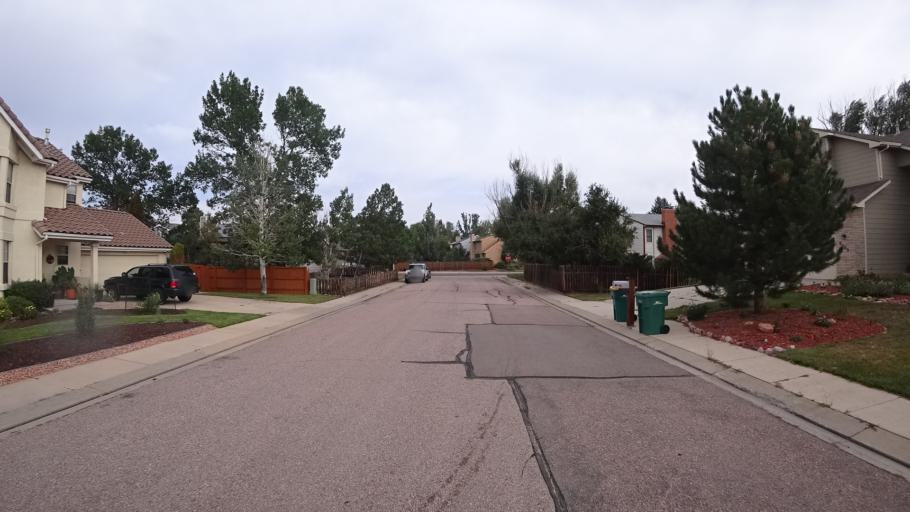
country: US
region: Colorado
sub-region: El Paso County
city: Air Force Academy
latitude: 38.9215
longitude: -104.8317
